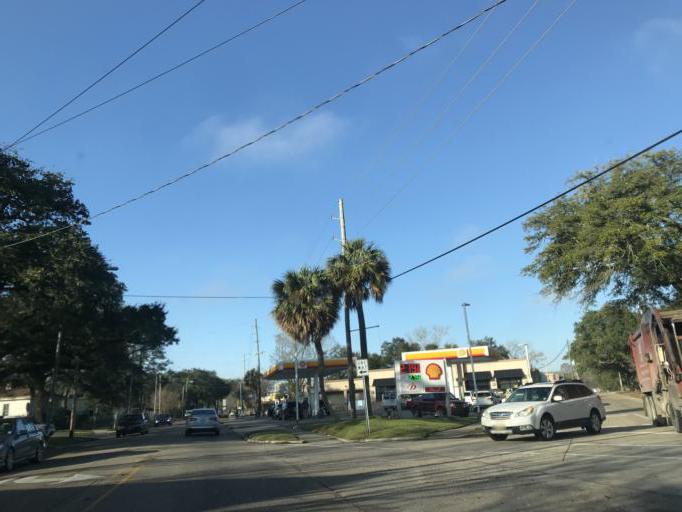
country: US
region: Louisiana
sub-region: Jefferson Parish
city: Metairie
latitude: 29.9879
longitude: -90.1383
